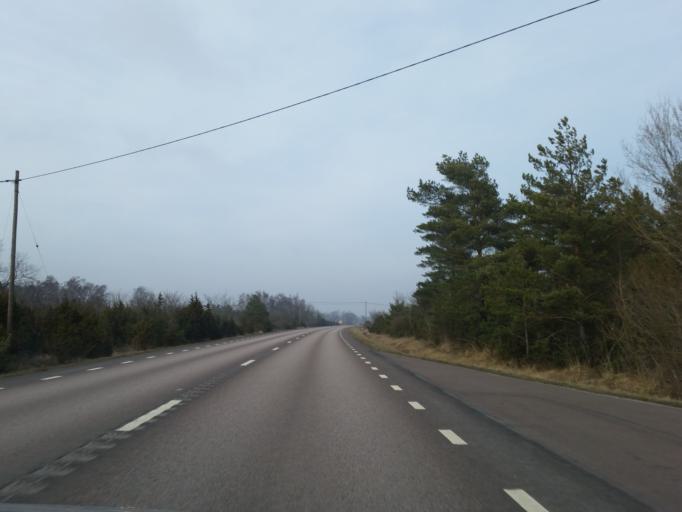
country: SE
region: Kalmar
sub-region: Borgholms Kommun
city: Borgholm
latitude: 57.0979
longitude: 16.9303
